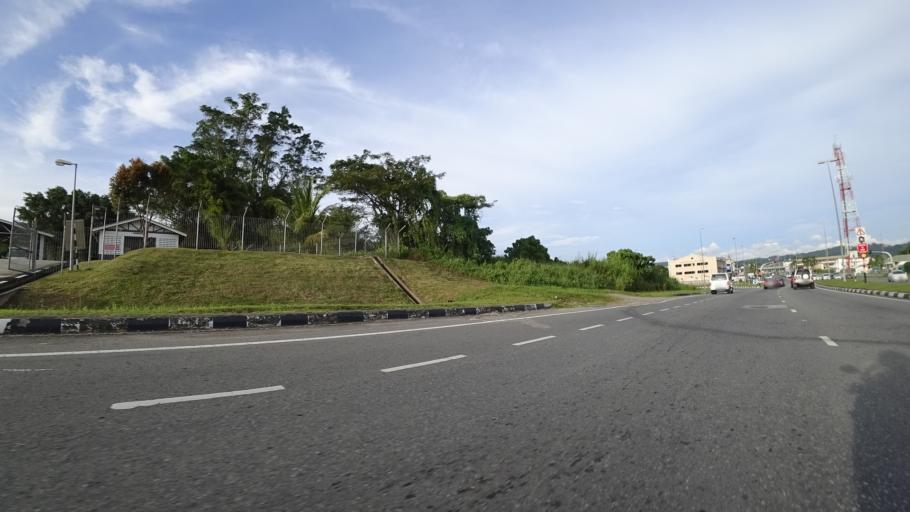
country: BN
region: Brunei and Muara
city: Bandar Seri Begawan
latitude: 4.8850
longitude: 114.8378
